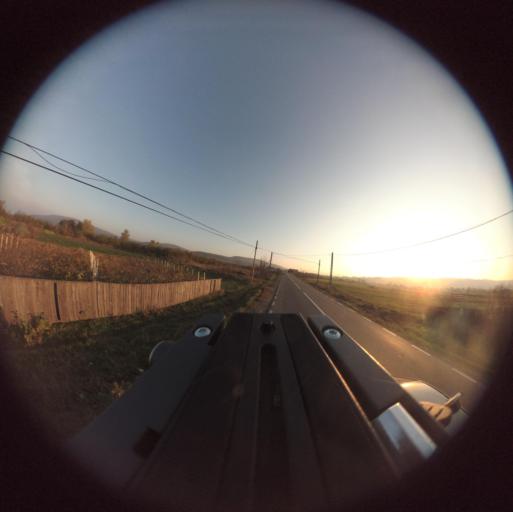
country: RO
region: Vaslui
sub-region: Comuna Bacesti
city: Bacesti
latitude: 46.8314
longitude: 27.2520
